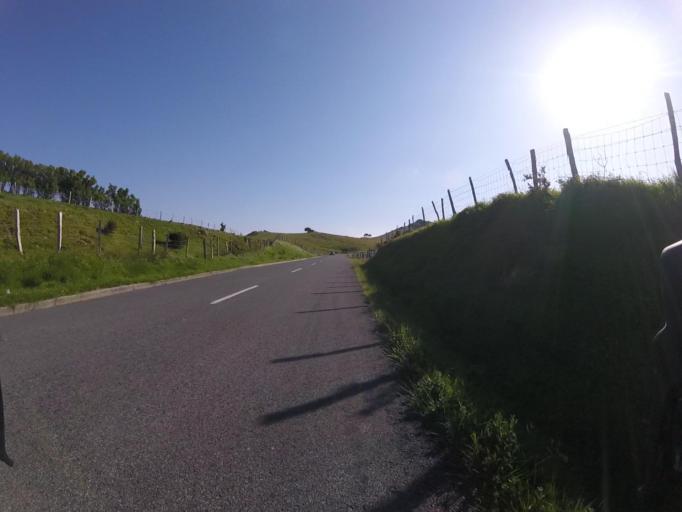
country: ES
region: Basque Country
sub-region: Provincia de Guipuzcoa
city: Fuenterrabia
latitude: 43.3533
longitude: -1.8428
